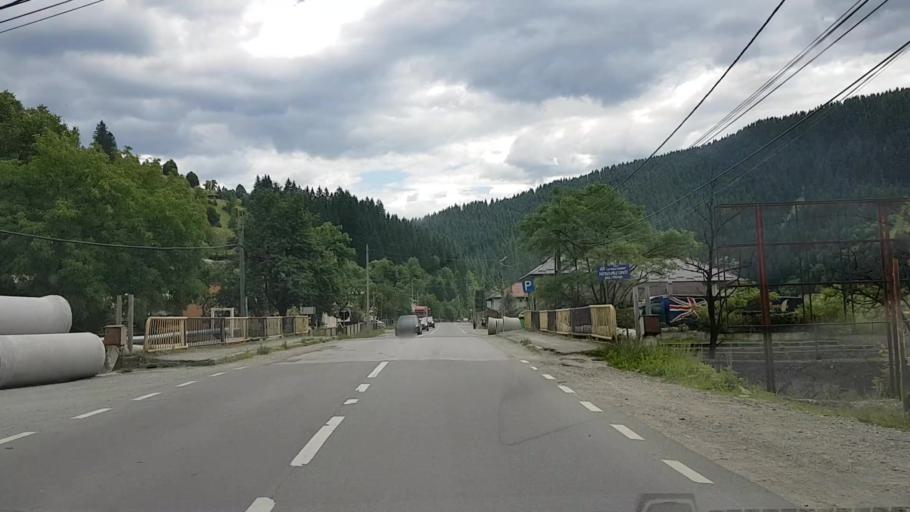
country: RO
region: Neamt
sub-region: Comuna Farcasa
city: Farcasa
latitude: 47.1560
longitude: 25.8396
